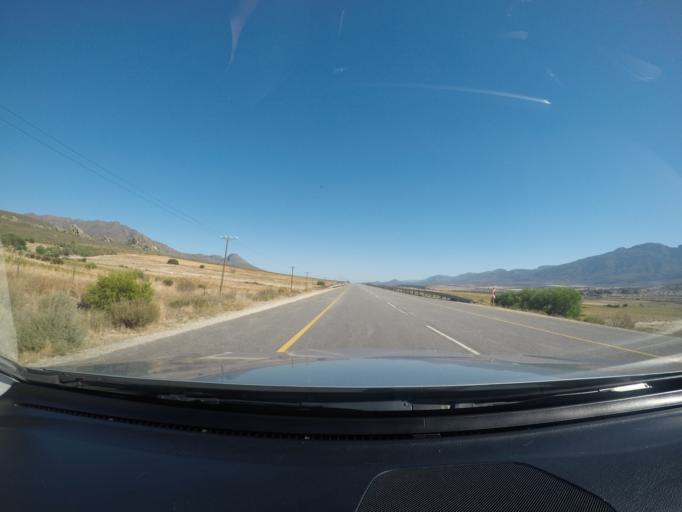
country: ZA
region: Western Cape
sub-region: West Coast District Municipality
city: Piketberg
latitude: -32.5861
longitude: 18.9888
